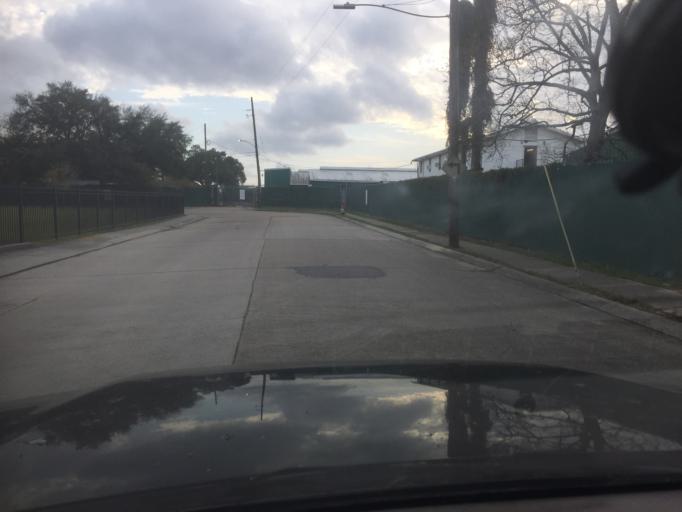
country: US
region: Louisiana
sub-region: Orleans Parish
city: New Orleans
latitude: 29.9885
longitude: -90.0834
